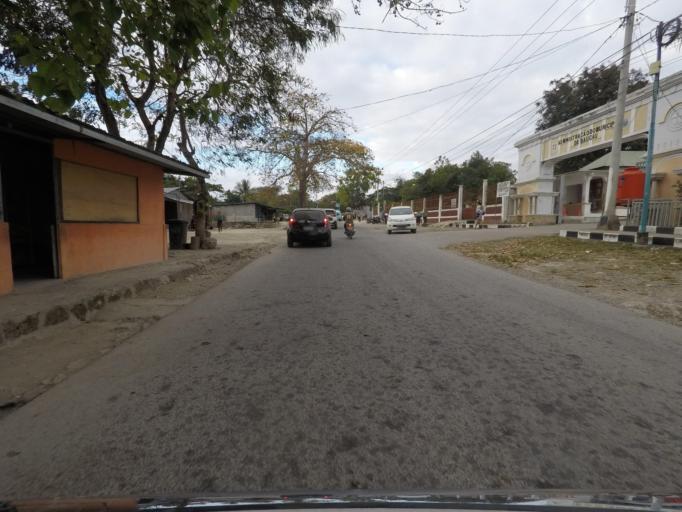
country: TL
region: Baucau
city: Baucau
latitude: -8.4726
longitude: 126.4584
